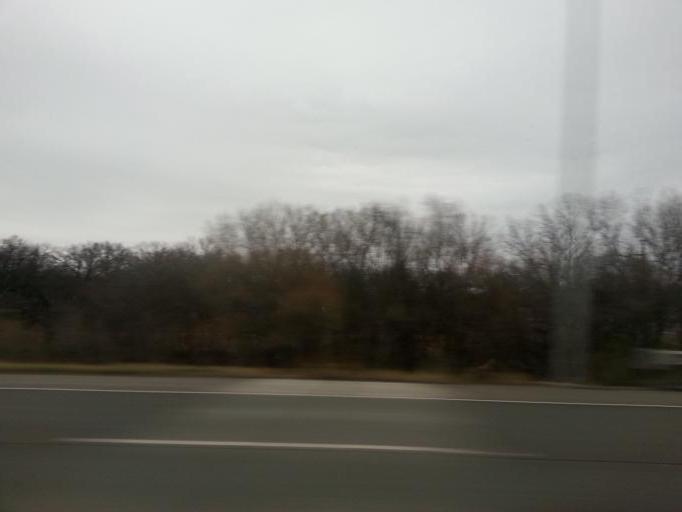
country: US
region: Iowa
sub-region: Linn County
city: Cedar Rapids
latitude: 42.0003
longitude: -91.6665
